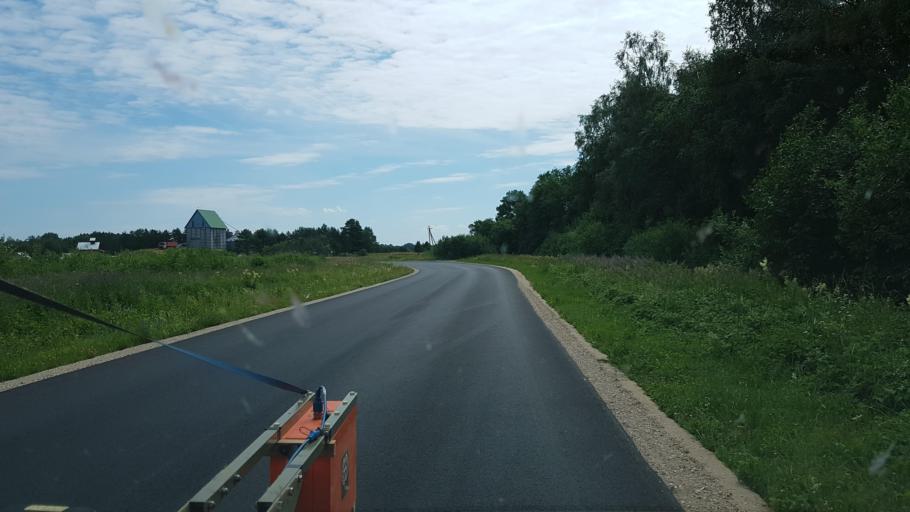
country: EE
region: Paernumaa
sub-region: Halinga vald
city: Parnu-Jaagupi
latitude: 58.6196
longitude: 24.3263
